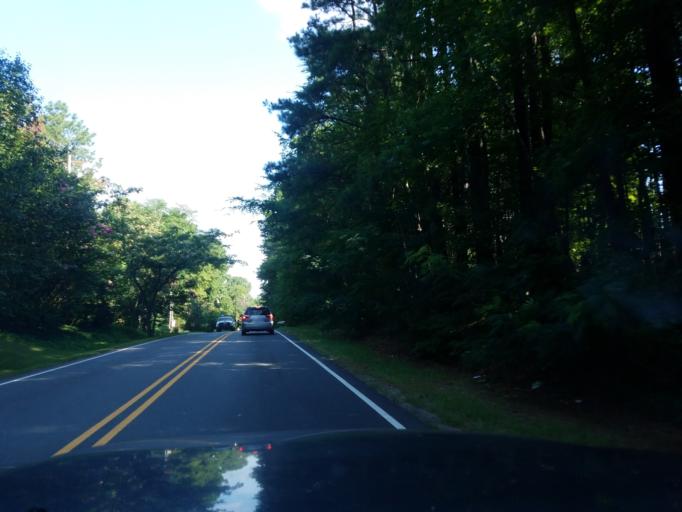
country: US
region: North Carolina
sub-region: Durham County
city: Durham
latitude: 35.9437
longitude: -78.9669
